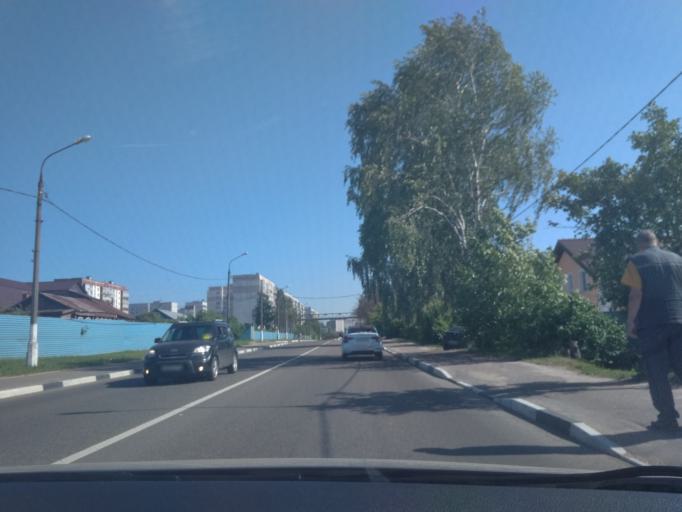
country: RU
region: Moskovskaya
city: Orekhovo-Zuyevo
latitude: 55.8038
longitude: 38.9782
